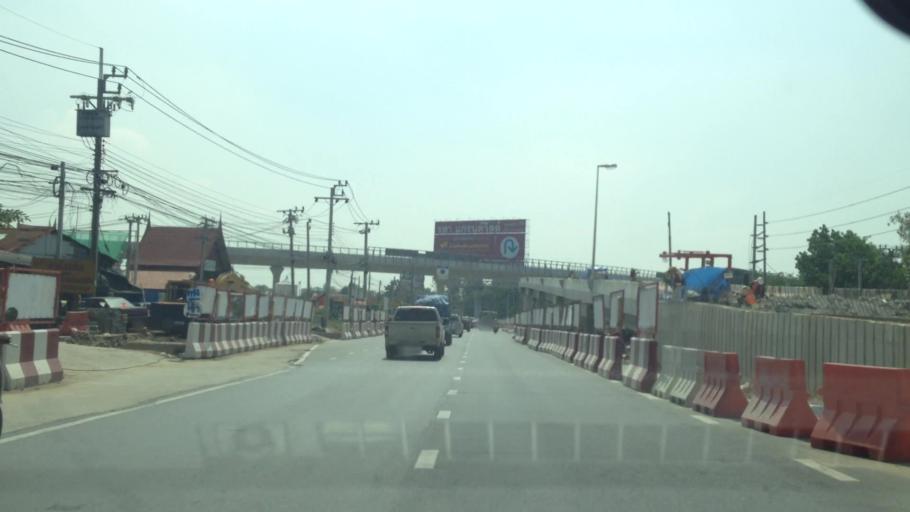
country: TH
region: Bangkok
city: Sai Mai
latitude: 13.9285
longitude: 100.6264
